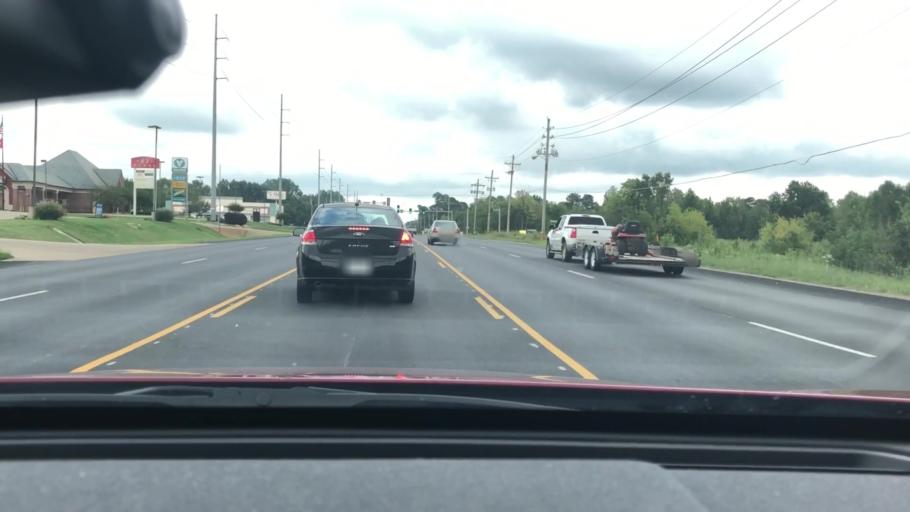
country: US
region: Arkansas
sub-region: Miller County
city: Texarkana
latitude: 33.4305
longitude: -94.0018
